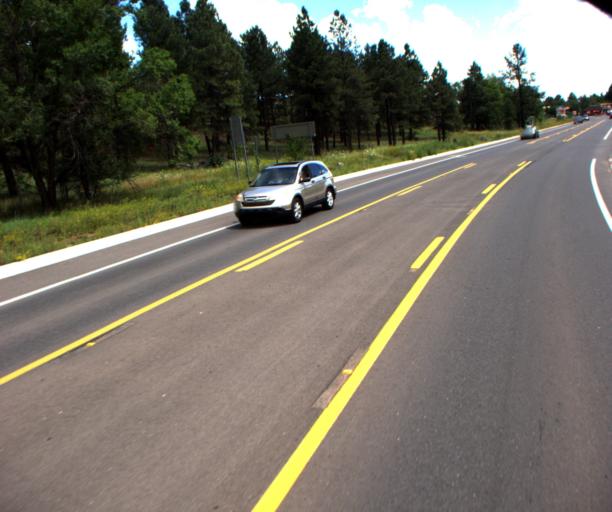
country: US
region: Arizona
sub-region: Coconino County
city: Flagstaff
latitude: 35.2099
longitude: -111.6488
